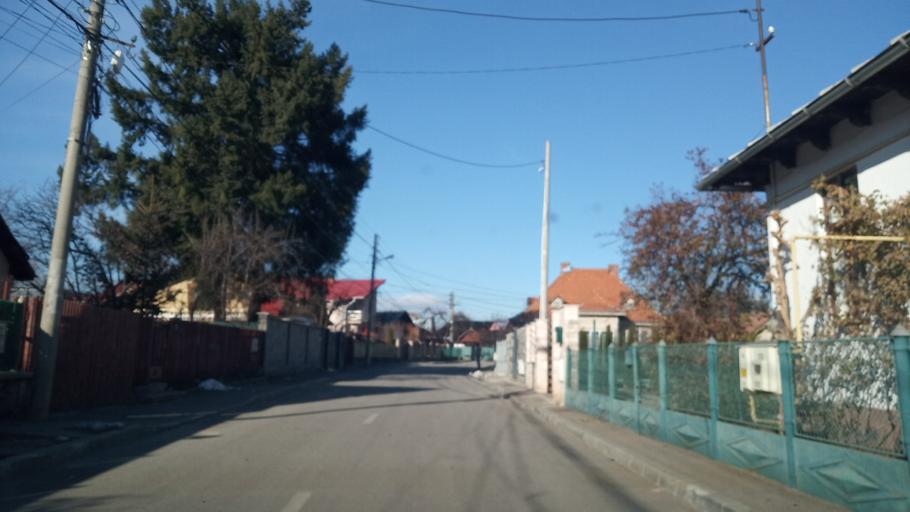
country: RO
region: Prahova
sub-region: Oras Breaza
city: Breaza
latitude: 45.1869
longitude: 25.6666
